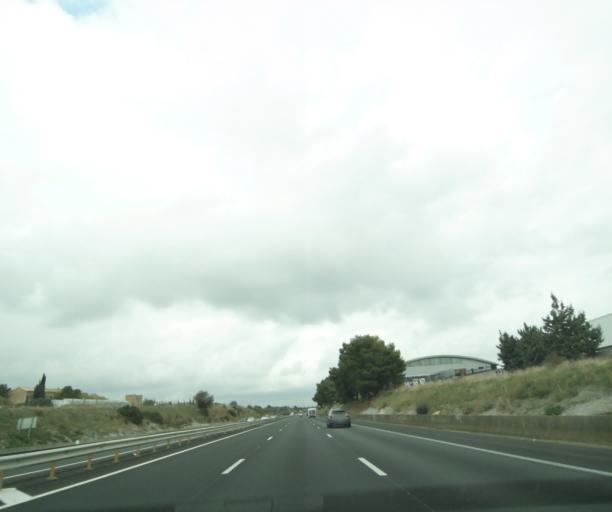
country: FR
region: Languedoc-Roussillon
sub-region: Departement de l'Herault
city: Meze
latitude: 43.4432
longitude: 3.5734
